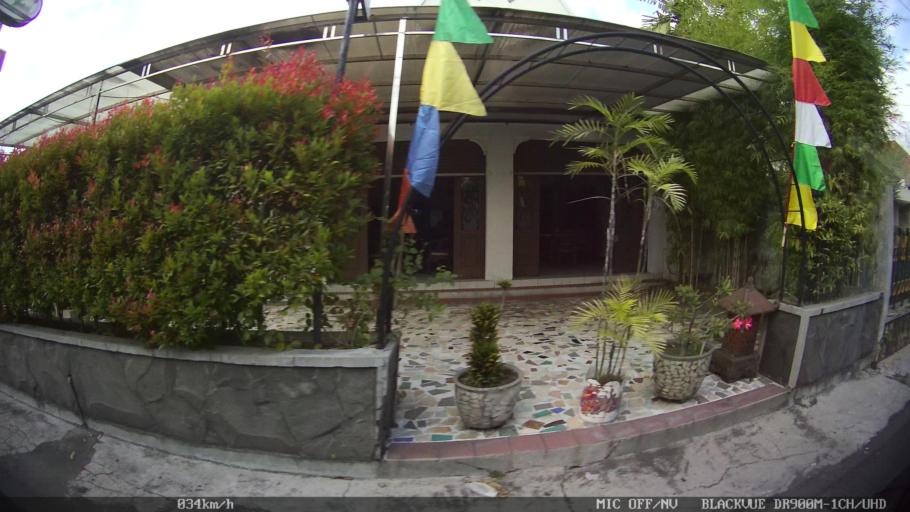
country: ID
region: Daerah Istimewa Yogyakarta
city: Yogyakarta
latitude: -7.8187
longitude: 110.3664
